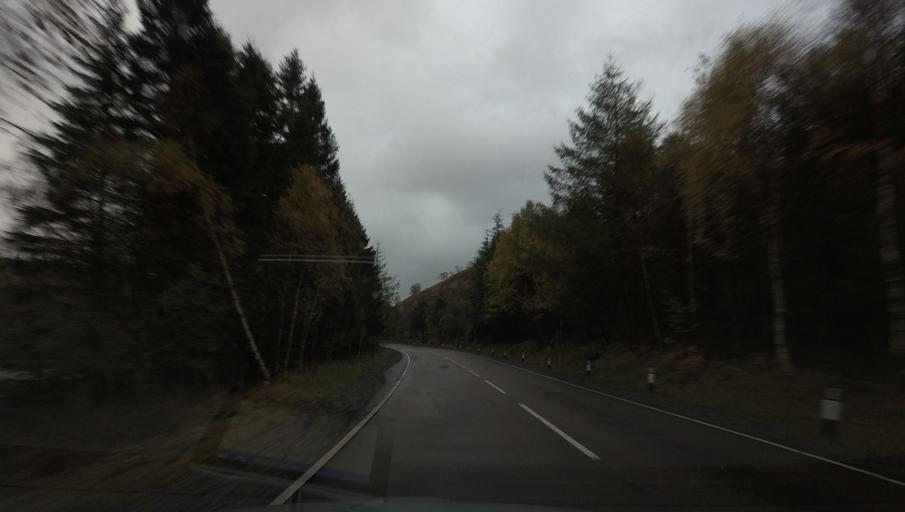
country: GB
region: Scotland
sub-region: Stirling
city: Callander
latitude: 56.4093
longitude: -4.5405
